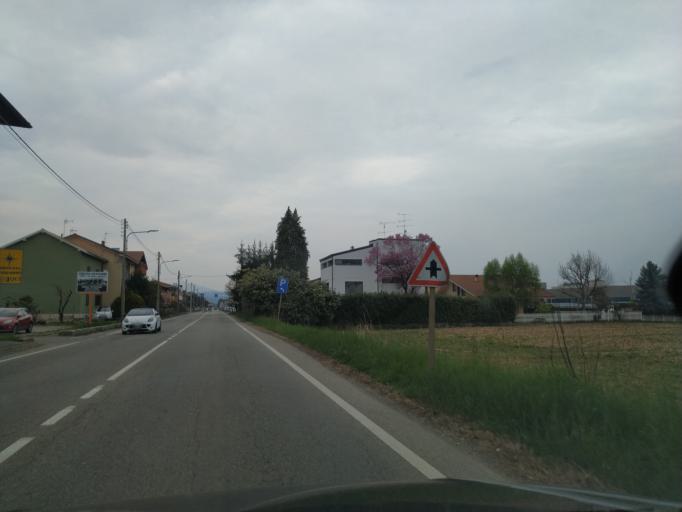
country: IT
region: Piedmont
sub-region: Provincia di Novara
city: Cureggio
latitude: 45.6763
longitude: 8.4561
